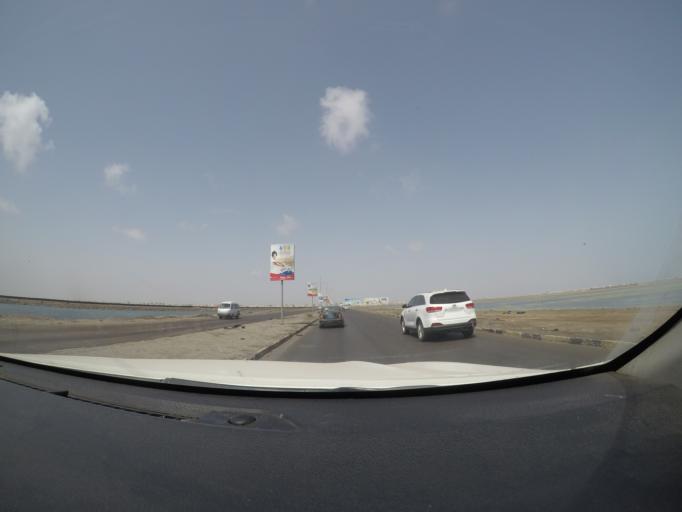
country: YE
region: Aden
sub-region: Khur Maksar
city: Khawr Maksar
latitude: 12.8303
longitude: 45.0305
